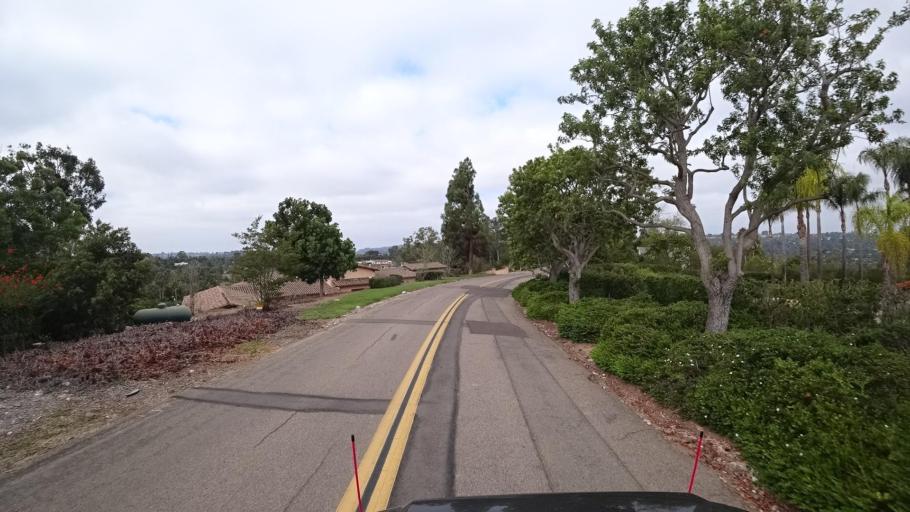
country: US
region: California
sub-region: San Diego County
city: Rancho Santa Fe
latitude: 33.0413
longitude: -117.2174
